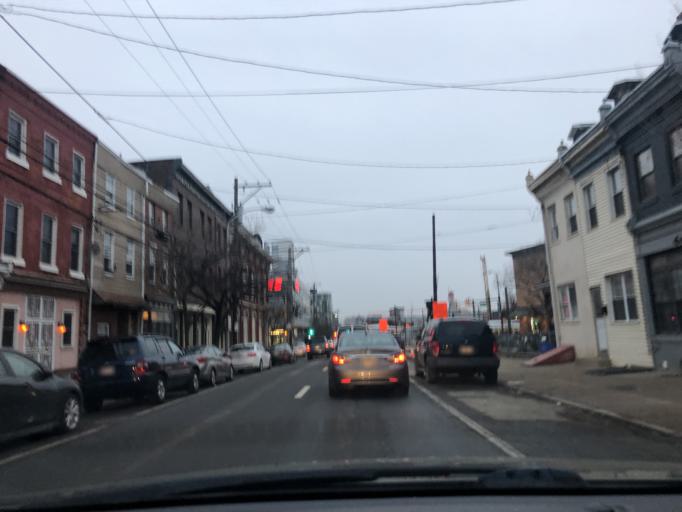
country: US
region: Pennsylvania
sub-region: Philadelphia County
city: Philadelphia
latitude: 39.9703
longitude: -75.1394
